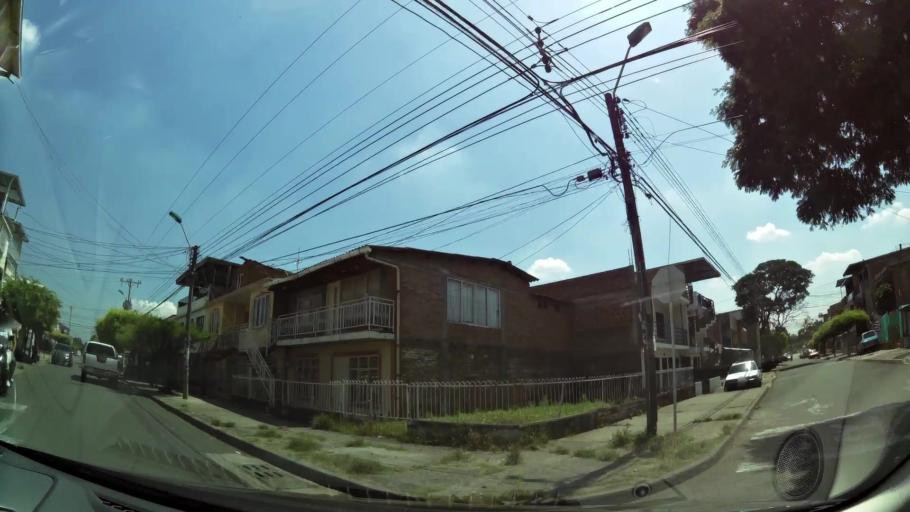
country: CO
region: Valle del Cauca
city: Cali
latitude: 3.4296
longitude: -76.5002
